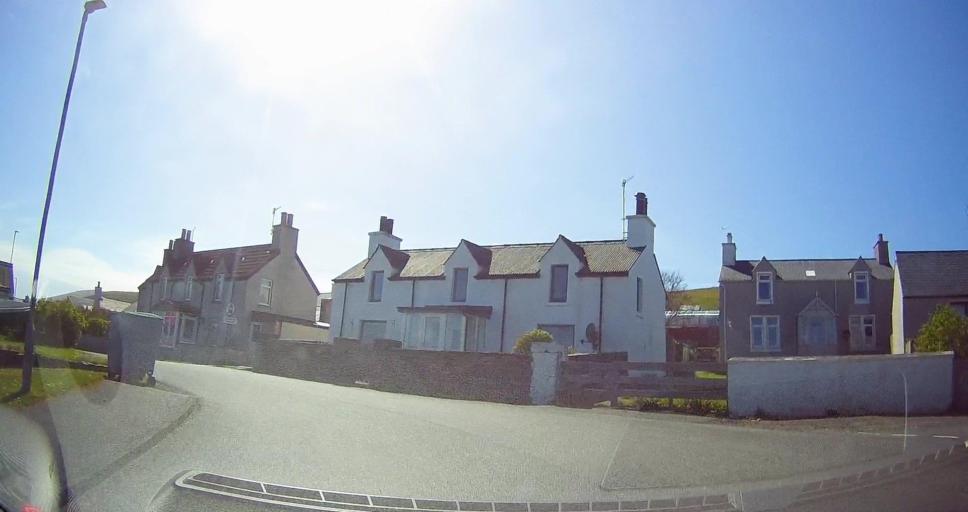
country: GB
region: Scotland
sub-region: Shetland Islands
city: Sandwick
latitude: 59.9984
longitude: -1.2544
